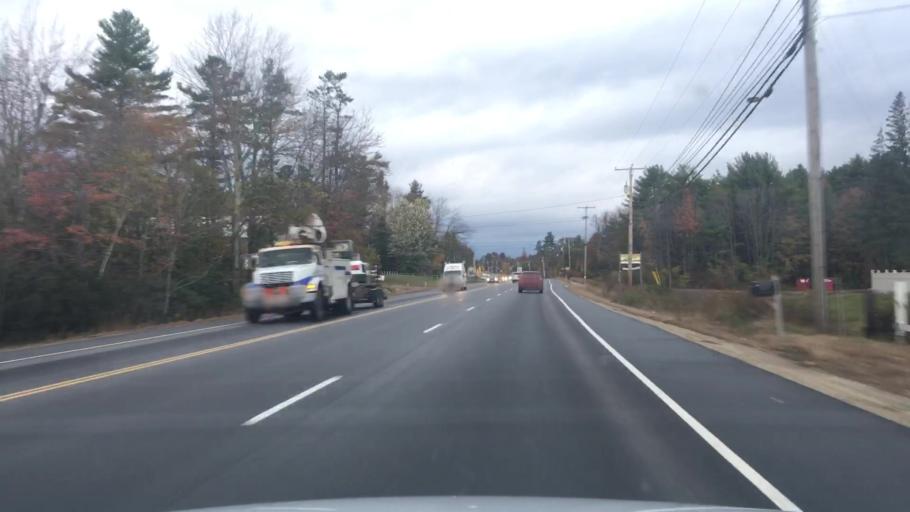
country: US
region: New Hampshire
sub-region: Merrimack County
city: Chichester
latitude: 43.2391
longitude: -71.3944
